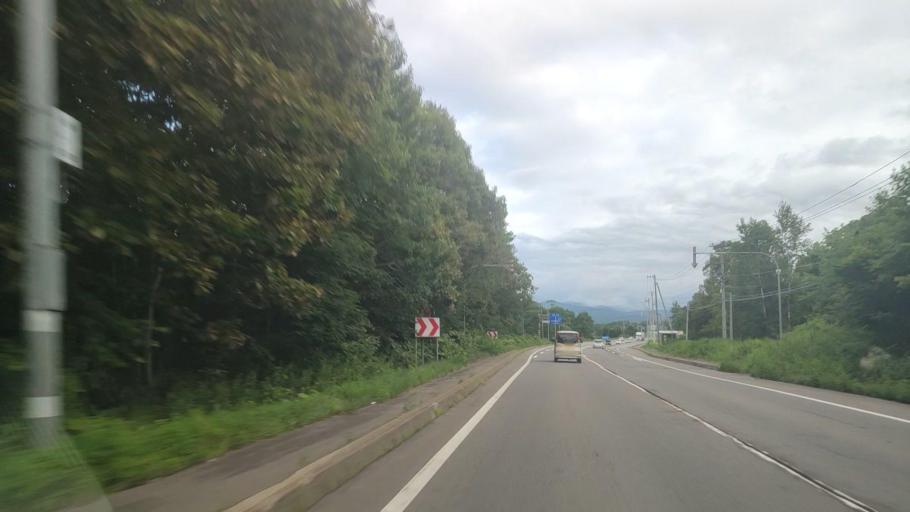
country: JP
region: Hokkaido
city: Nanae
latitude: 42.0110
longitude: 140.6286
